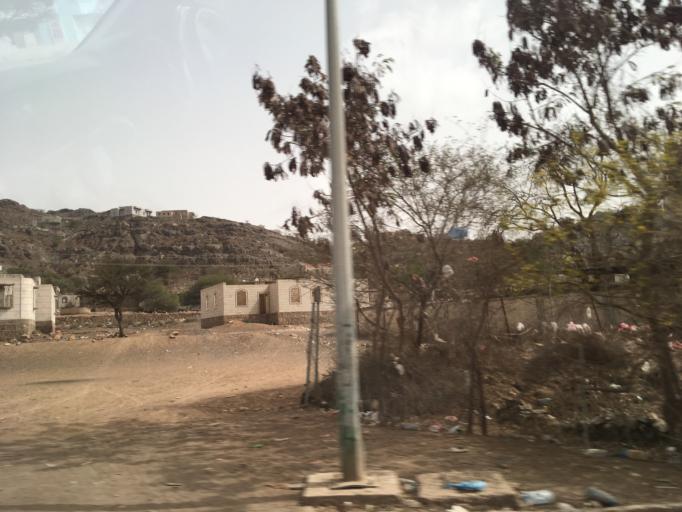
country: YE
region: Ad Dali'
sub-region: Ad Dhale'e
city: Dhalie
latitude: 13.7042
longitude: 44.7368
